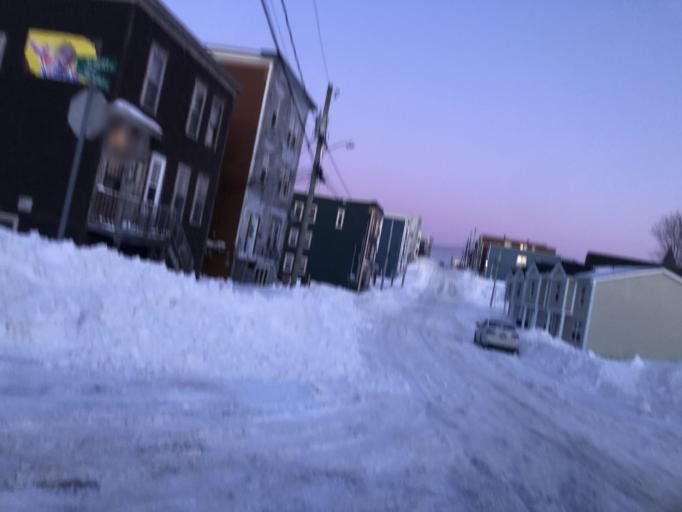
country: CA
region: New Brunswick
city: Saint John
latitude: 45.2761
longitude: -66.0845
